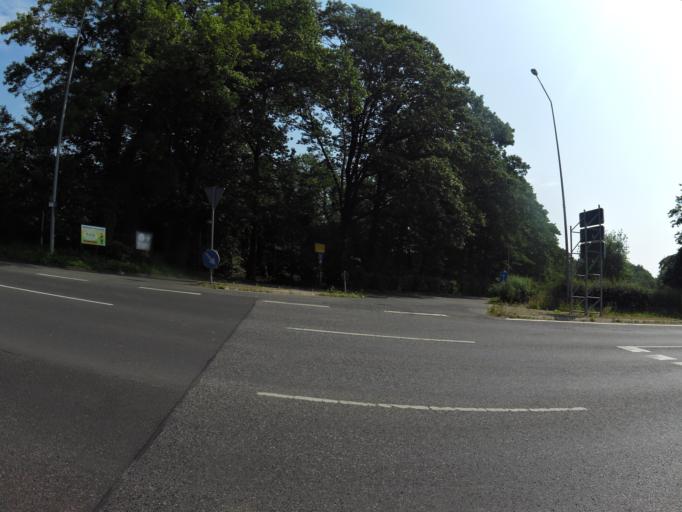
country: DE
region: North Rhine-Westphalia
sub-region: Regierungsbezirk Koln
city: Aachen
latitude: 50.8104
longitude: 6.0920
